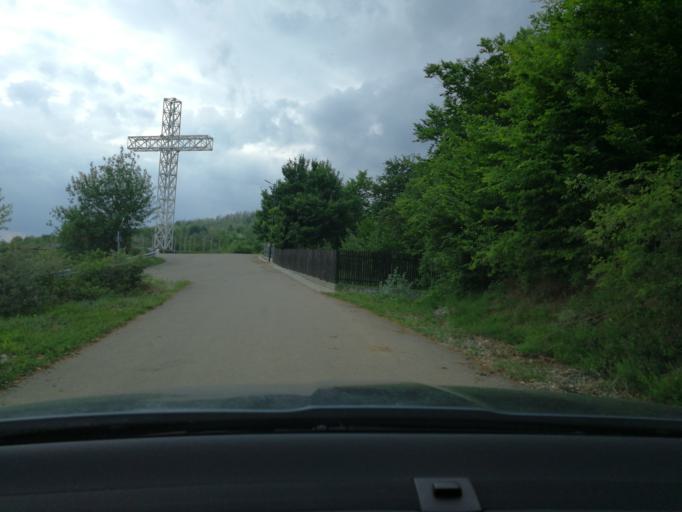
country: RO
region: Prahova
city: Cornu de Sus
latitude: 45.1724
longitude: 25.7074
